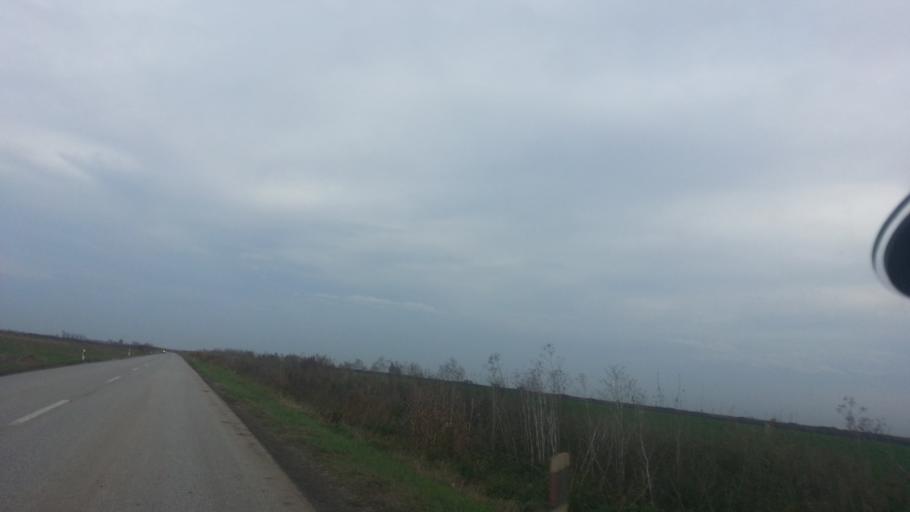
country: RS
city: Putinci
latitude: 44.9901
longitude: 19.9984
